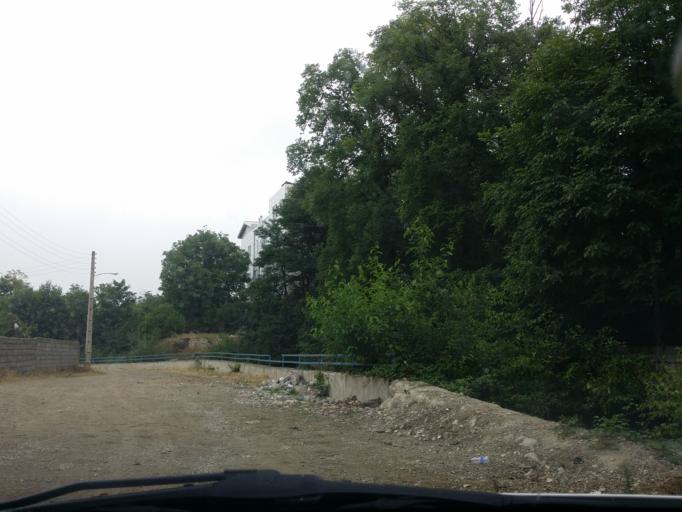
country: IR
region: Mazandaran
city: `Abbasabad
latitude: 36.5044
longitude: 51.1542
